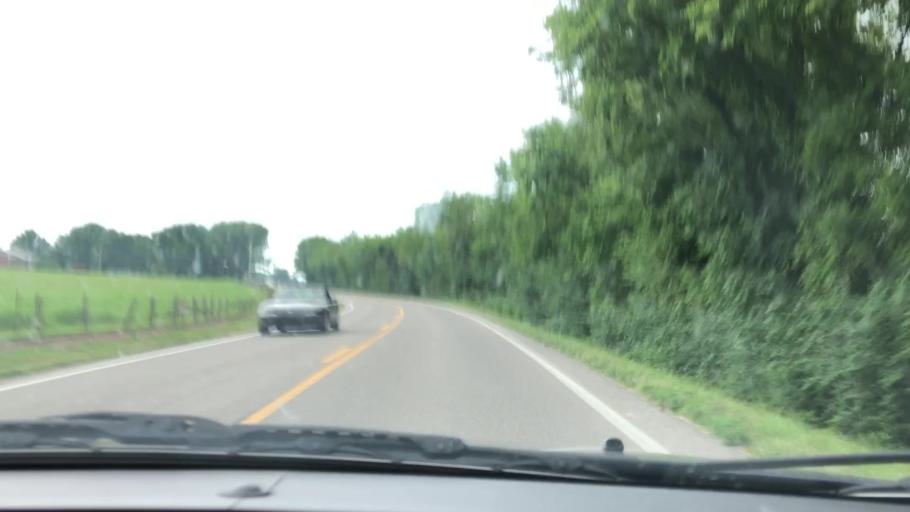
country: US
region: Tennessee
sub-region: Maury County
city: Spring Hill
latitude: 35.7626
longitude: -87.0070
